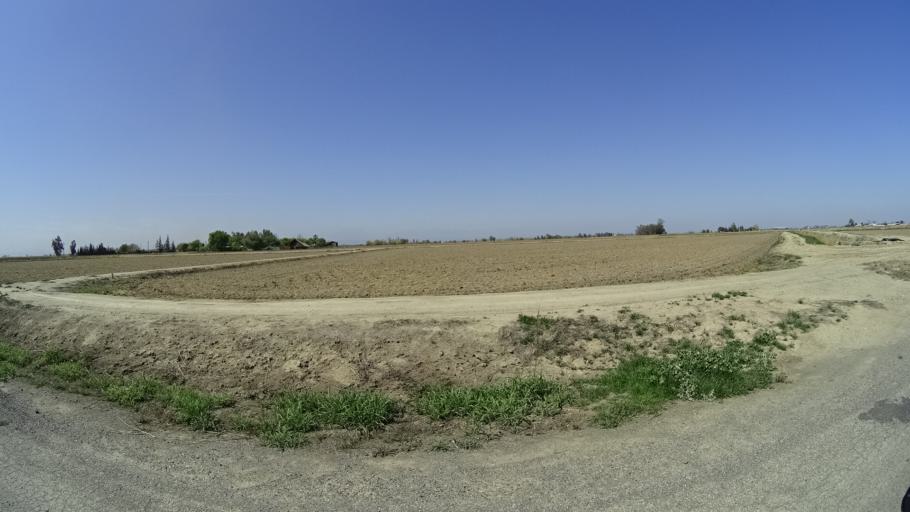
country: US
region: California
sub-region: Glenn County
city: Willows
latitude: 39.5256
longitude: -122.1121
